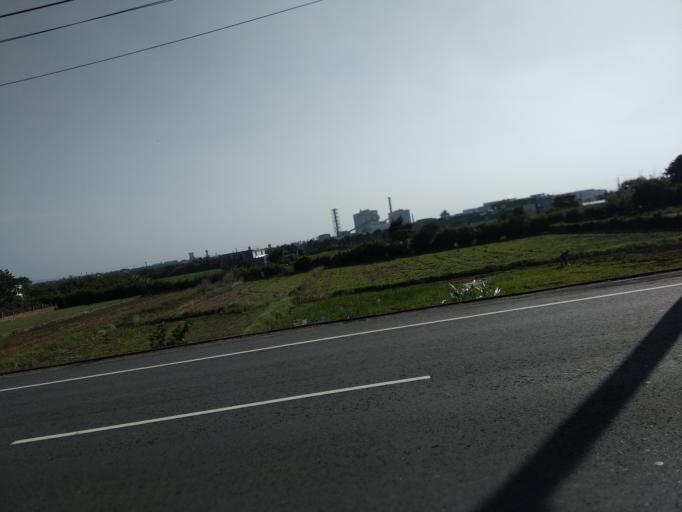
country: TW
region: Taiwan
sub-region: Hsinchu
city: Zhubei
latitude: 24.9868
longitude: 121.0477
